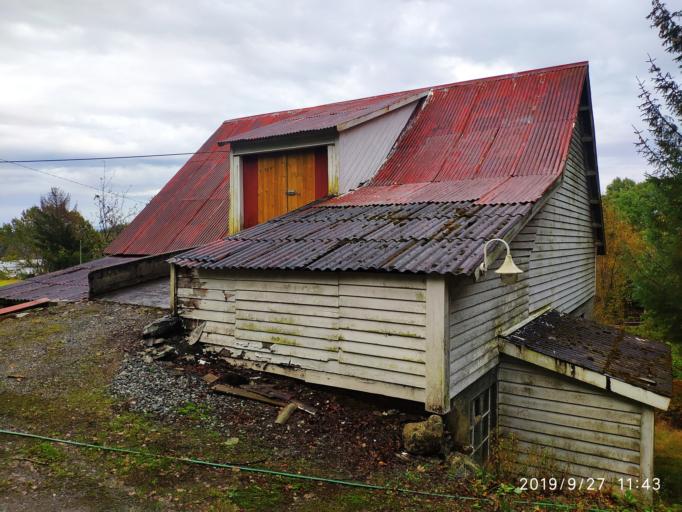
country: NO
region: Rogaland
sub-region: Karmoy
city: Kopervik
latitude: 59.2891
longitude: 5.3615
